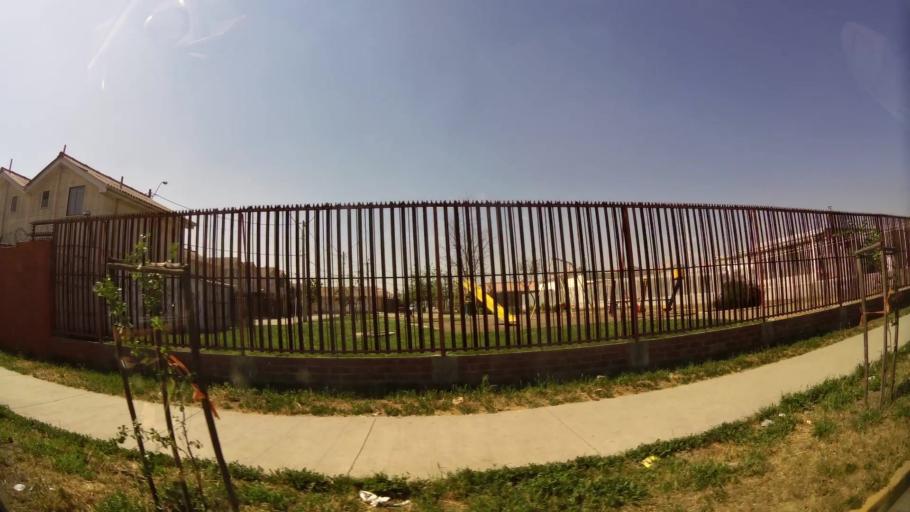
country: CL
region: Santiago Metropolitan
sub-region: Provincia de Talagante
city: Penaflor
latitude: -33.5752
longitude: -70.8063
